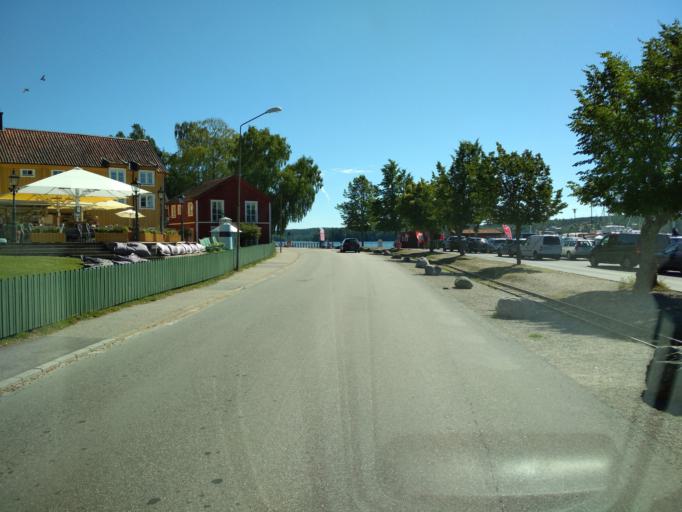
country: SE
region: Soedermanland
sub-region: Strangnas Kommun
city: Mariefred
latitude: 59.2579
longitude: 17.2219
